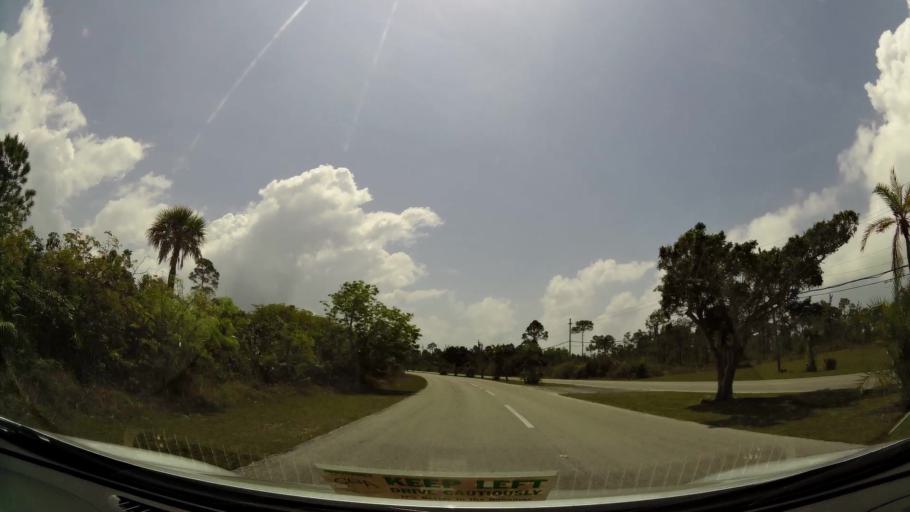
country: BS
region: Freeport
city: Lucaya
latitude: 26.5243
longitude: -78.6299
